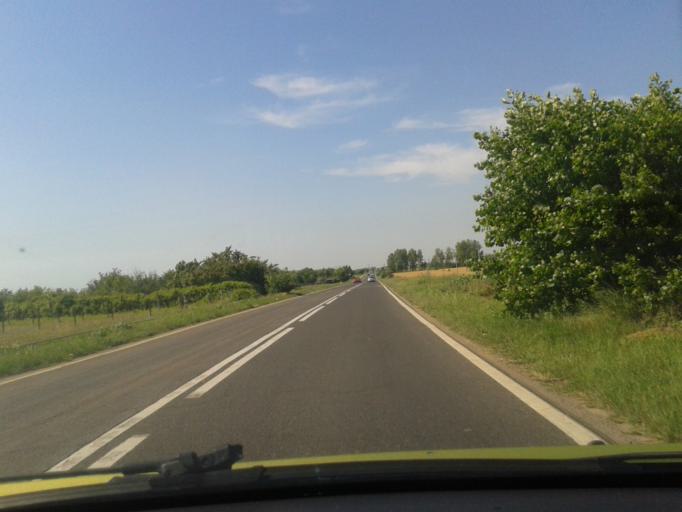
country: RO
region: Constanta
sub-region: Municipiul Mangalia
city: Mangalia
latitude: 43.7766
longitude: 28.5780
